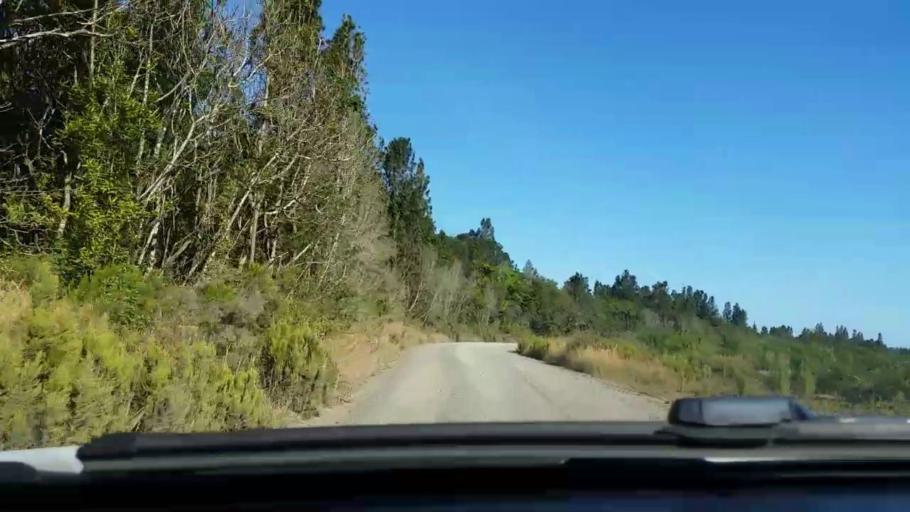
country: NZ
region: Bay of Plenty
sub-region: Kawerau District
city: Kawerau
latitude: -37.9961
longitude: 176.5385
